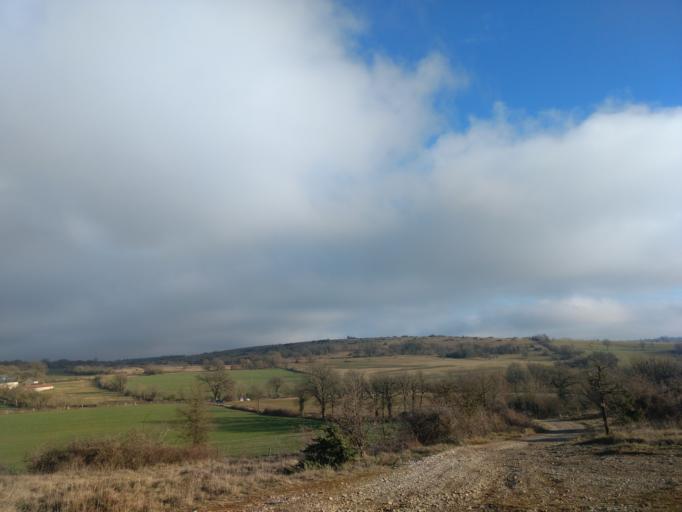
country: FR
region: Midi-Pyrenees
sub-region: Departement de l'Aveyron
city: Salles-la-Source
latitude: 44.4349
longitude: 2.5256
